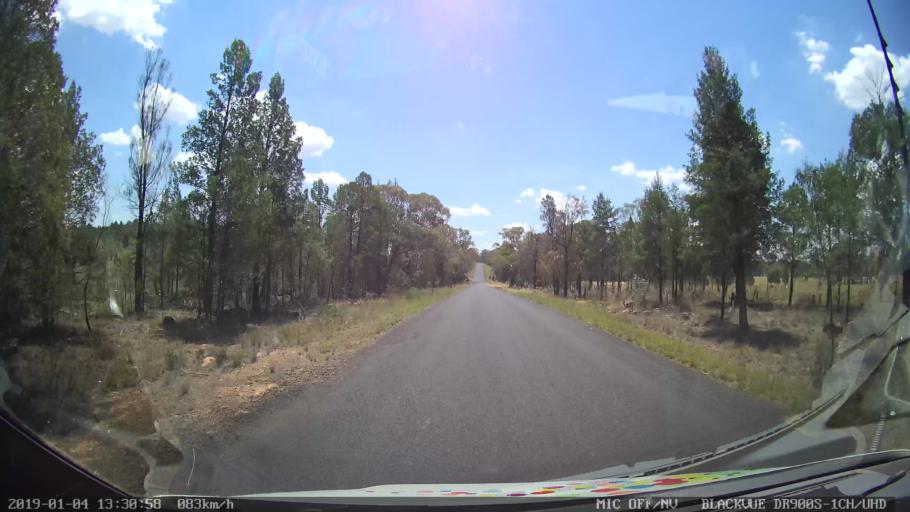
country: AU
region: New South Wales
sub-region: Parkes
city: Peak Hill
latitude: -32.6286
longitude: 148.5491
